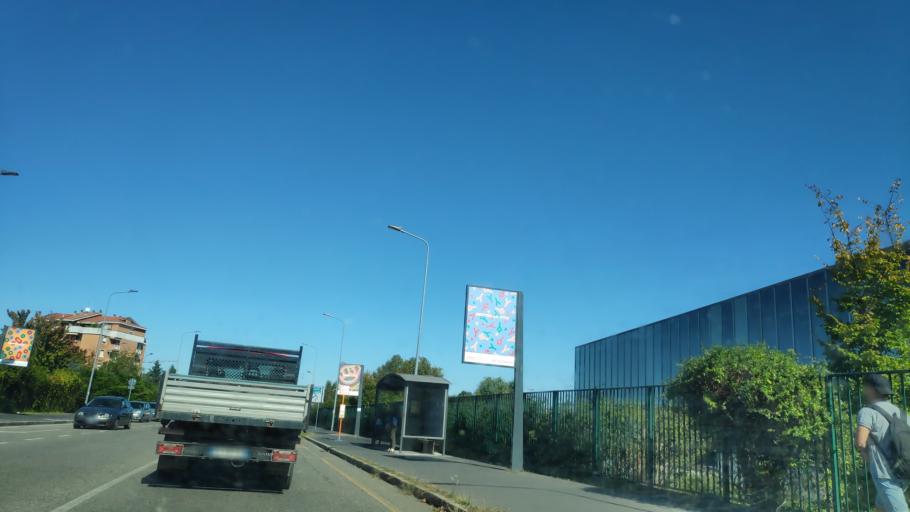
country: IT
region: Lombardy
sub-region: Citta metropolitana di Milano
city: Rozzano
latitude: 45.3721
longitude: 9.1680
